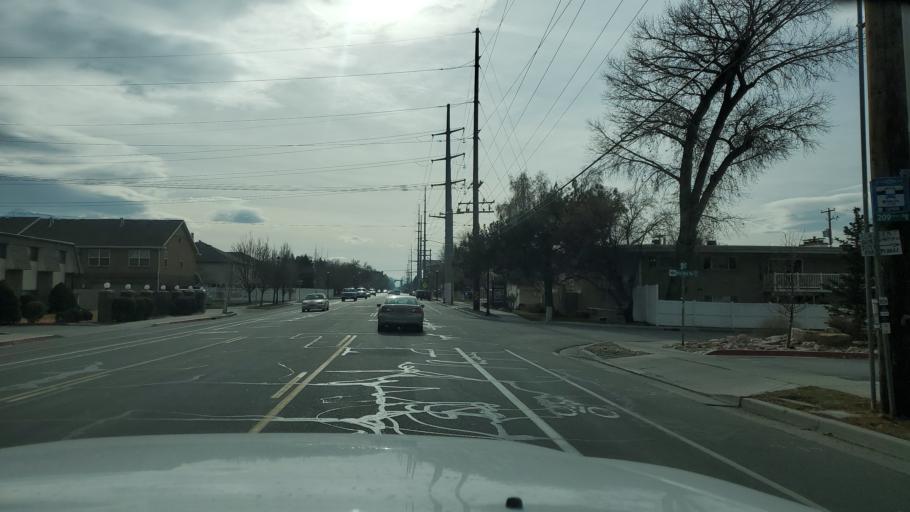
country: US
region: Utah
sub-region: Salt Lake County
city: Millcreek
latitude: 40.6900
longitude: -111.8656
